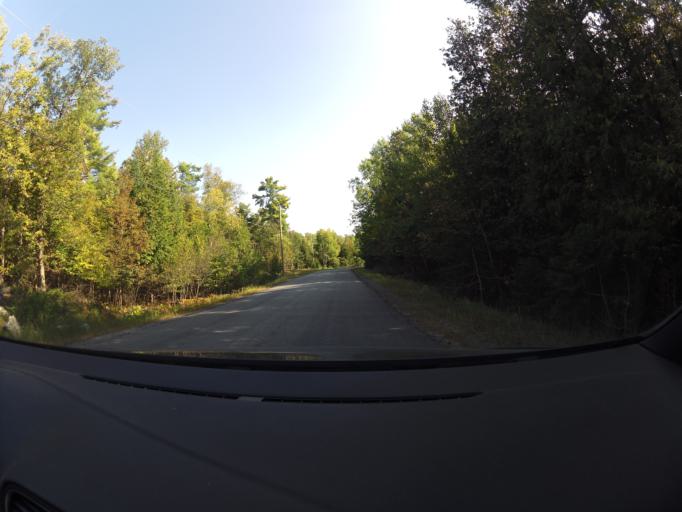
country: CA
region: Ontario
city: Arnprior
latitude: 45.4600
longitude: -76.2768
